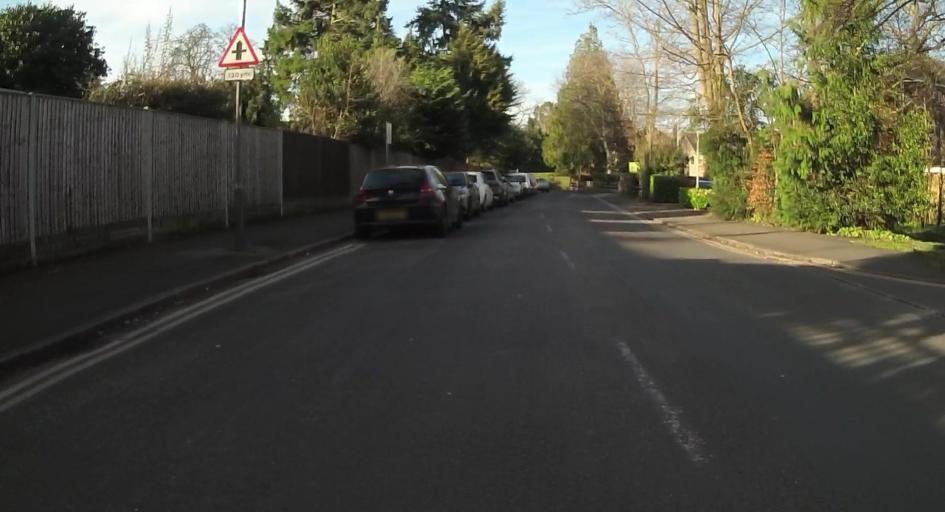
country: GB
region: England
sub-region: Surrey
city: Walton-on-Thames
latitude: 51.3743
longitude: -0.4158
